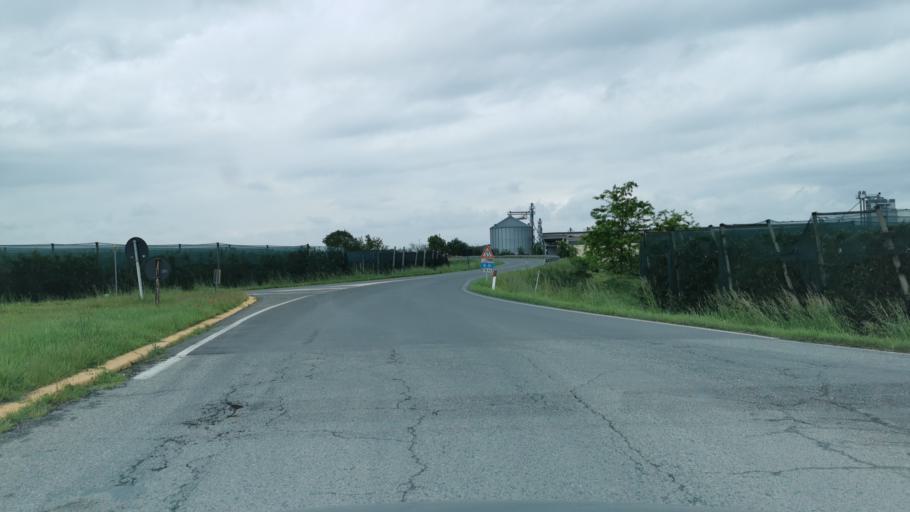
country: IT
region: Piedmont
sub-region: Provincia di Cuneo
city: Savigliano
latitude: 44.6409
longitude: 7.6458
